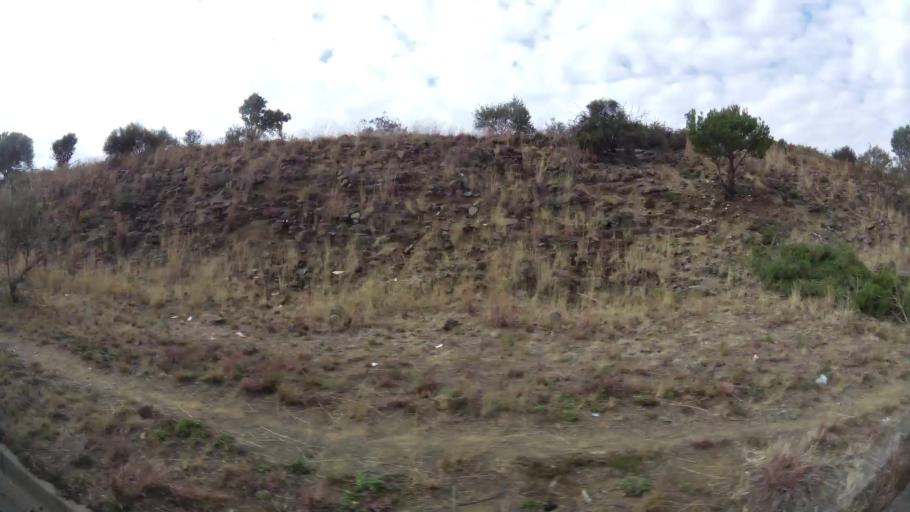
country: ZA
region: Orange Free State
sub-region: Mangaung Metropolitan Municipality
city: Bloemfontein
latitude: -29.1042
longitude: 26.2136
